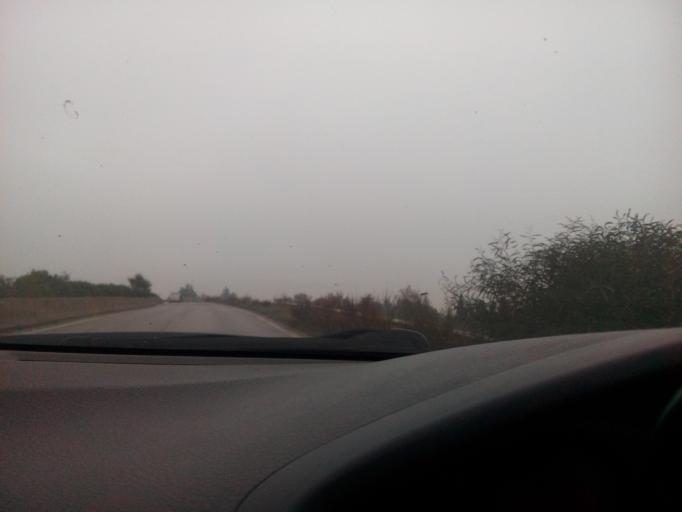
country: DZ
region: Oran
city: Bou Tlelis
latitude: 35.5668
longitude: -0.9067
